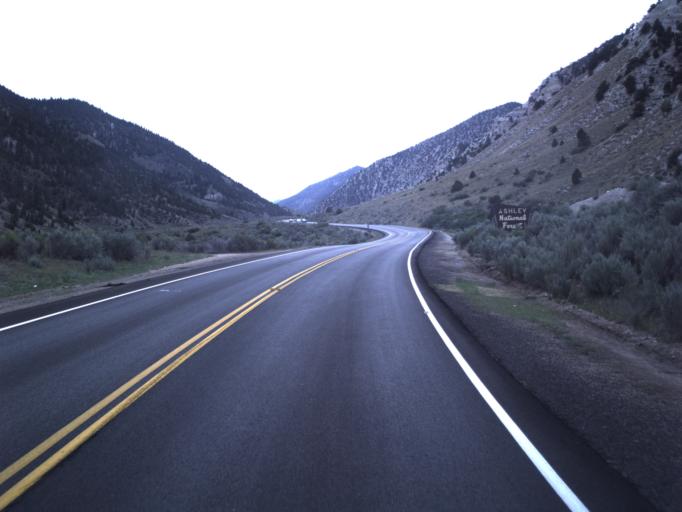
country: US
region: Utah
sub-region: Duchesne County
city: Duchesne
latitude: 39.9962
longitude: -110.5872
